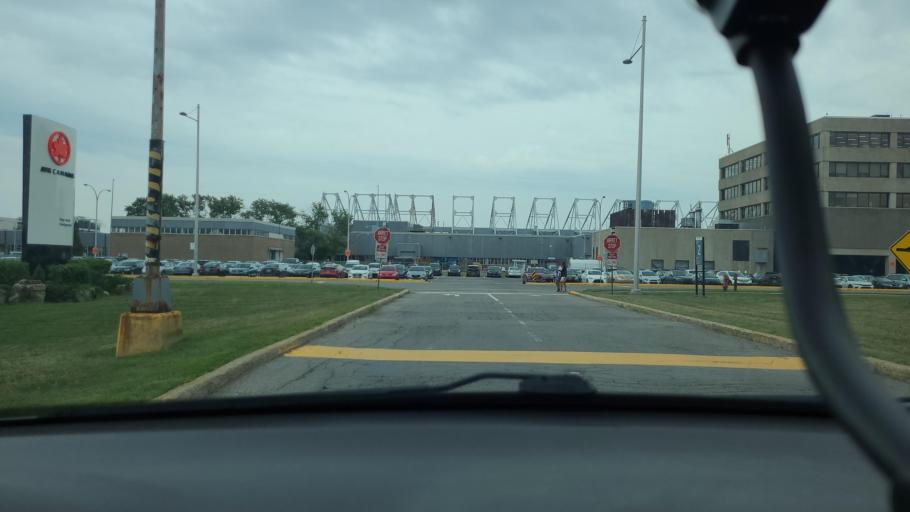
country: CA
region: Quebec
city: Dorval
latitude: 45.4725
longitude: -73.7362
